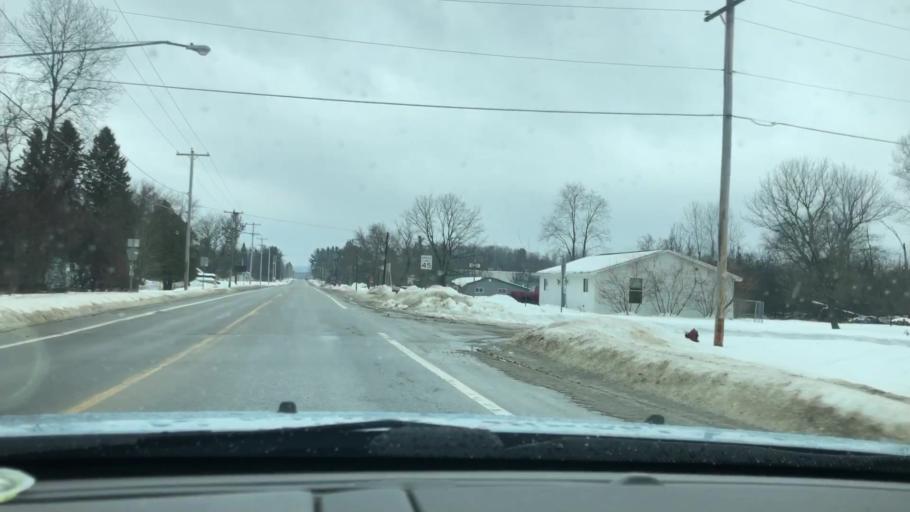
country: US
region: Michigan
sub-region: Charlevoix County
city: East Jordan
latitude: 45.1506
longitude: -85.1192
